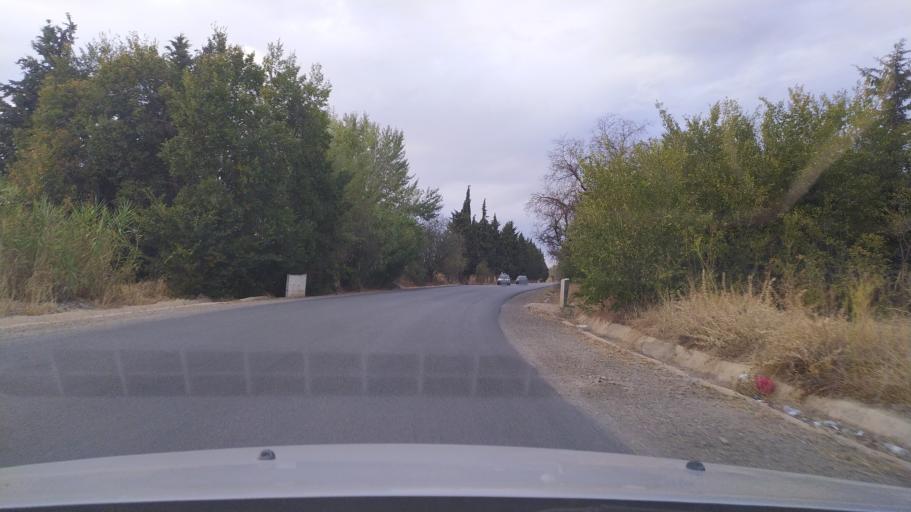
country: DZ
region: Tiaret
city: Frenda
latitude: 35.0311
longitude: 1.0919
